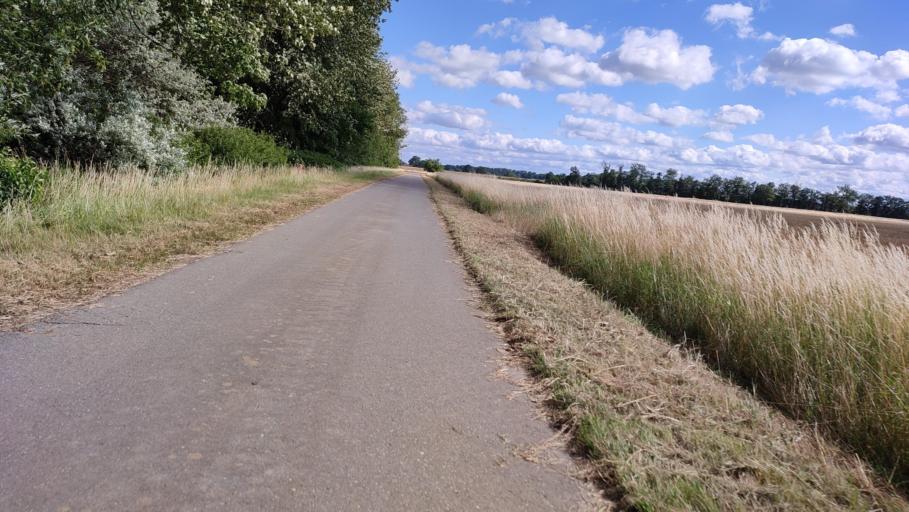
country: DE
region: Lower Saxony
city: Damnatz
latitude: 53.1822
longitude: 11.1466
